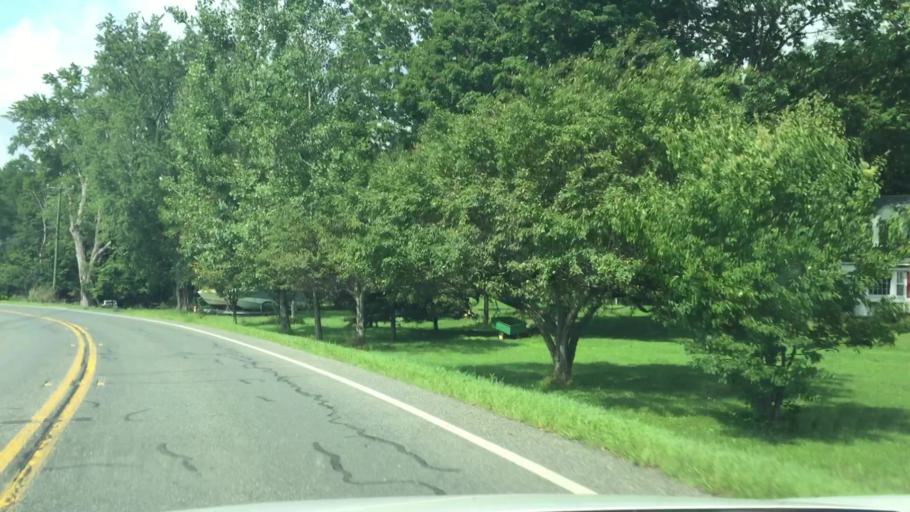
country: US
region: Massachusetts
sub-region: Berkshire County
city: Richmond
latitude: 42.4098
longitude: -73.3495
